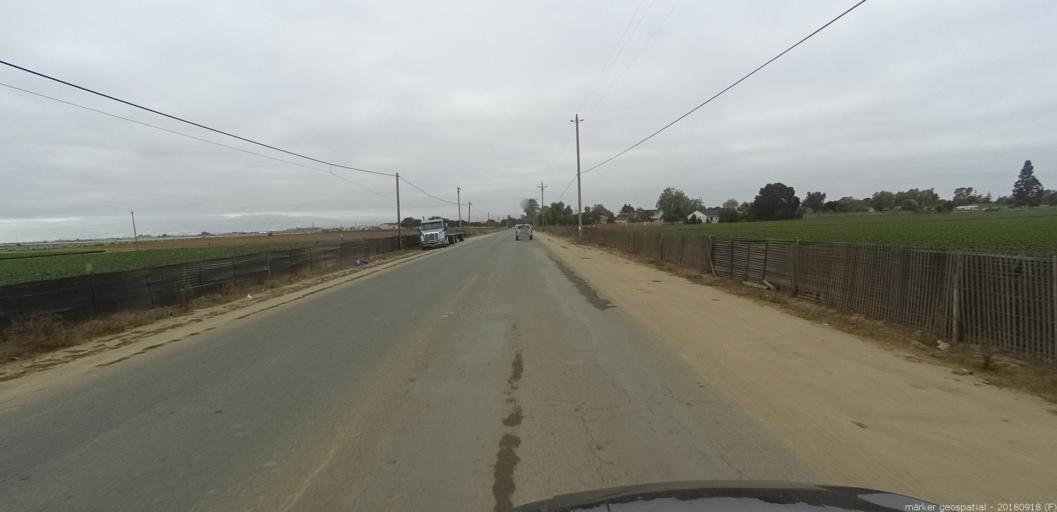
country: US
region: California
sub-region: Monterey County
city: Prunedale
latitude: 36.7496
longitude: -121.6245
